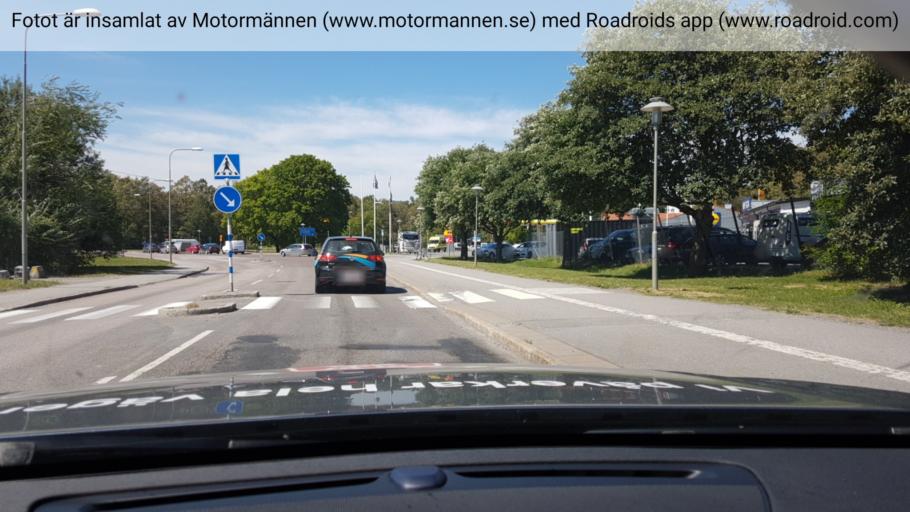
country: SE
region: Stockholm
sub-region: Huddinge Kommun
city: Huddinge
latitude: 59.2564
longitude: 18.0169
